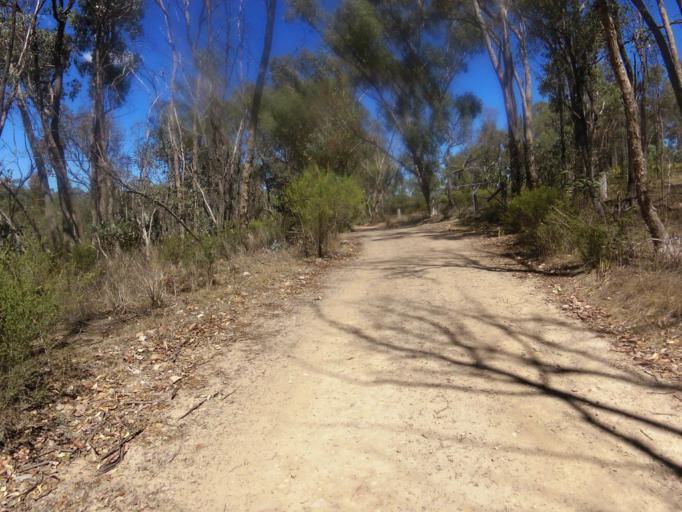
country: AU
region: Victoria
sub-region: Mount Alexander
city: Castlemaine
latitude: -37.0593
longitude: 144.1914
